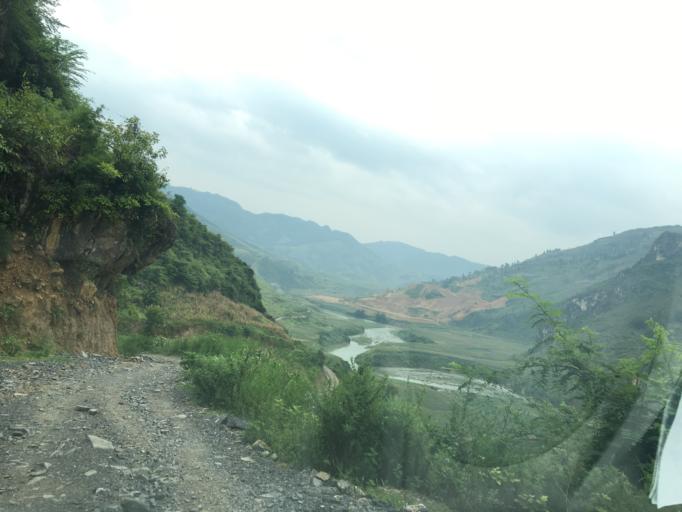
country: CN
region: Guangxi Zhuangzu Zizhiqu
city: Xinzhou
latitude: 25.1760
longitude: 105.7312
